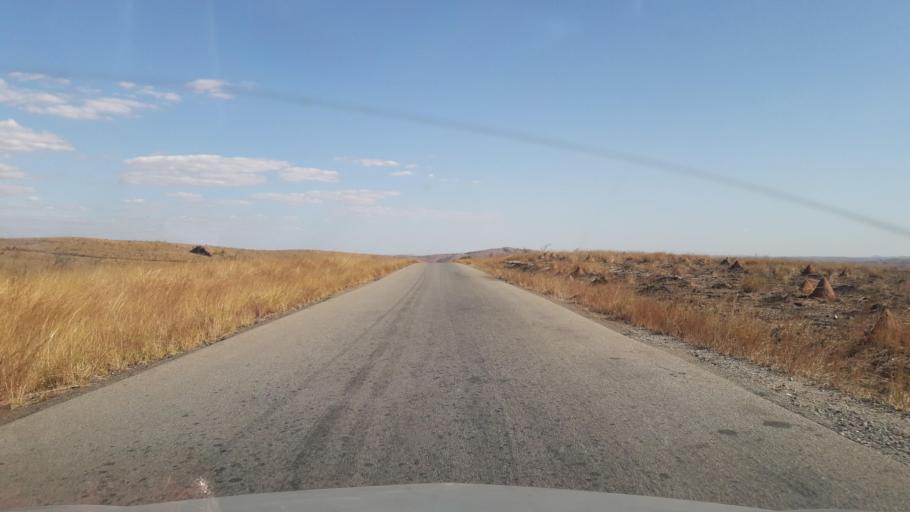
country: MG
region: Betsiboka
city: Maevatanana
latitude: -17.1533
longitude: 46.8374
